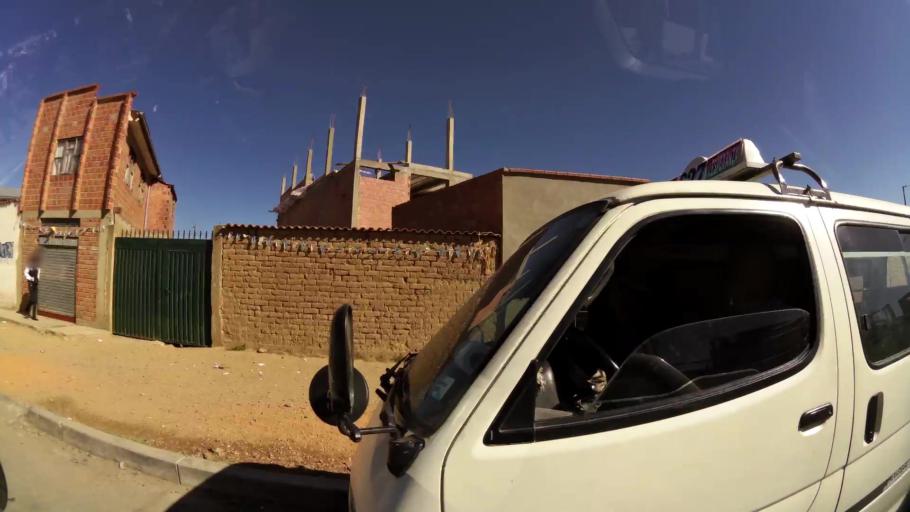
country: BO
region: La Paz
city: La Paz
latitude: -16.5304
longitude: -68.2203
